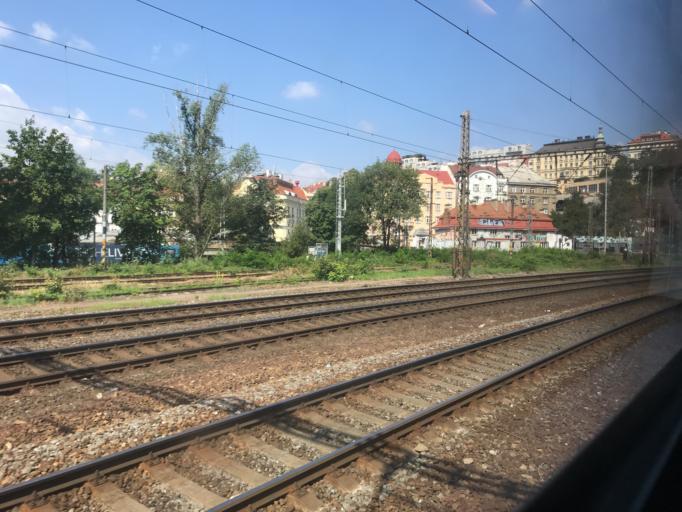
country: CZ
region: Praha
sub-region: Praha 2
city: Vysehrad
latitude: 50.0678
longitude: 14.4382
